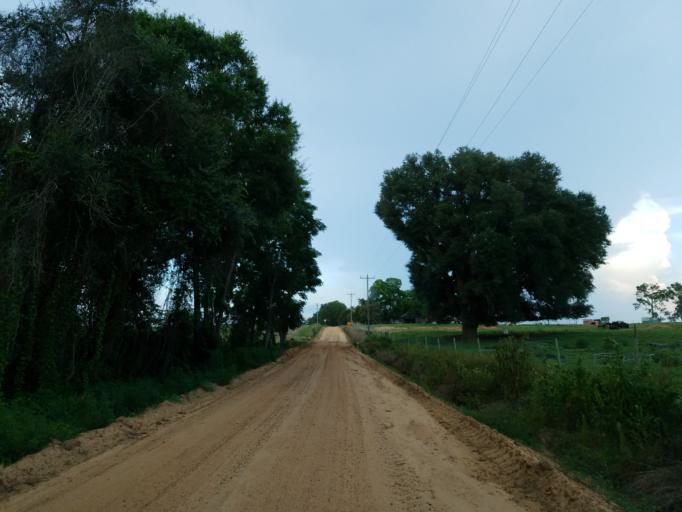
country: US
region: Georgia
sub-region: Tift County
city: Omega
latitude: 31.2741
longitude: -83.5216
